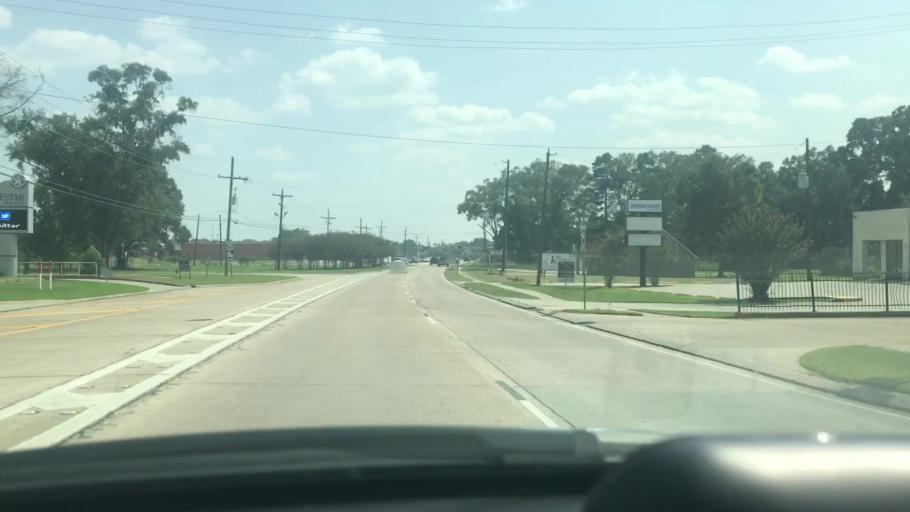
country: US
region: Louisiana
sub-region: Livingston Parish
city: Denham Springs
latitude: 30.4793
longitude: -90.9559
